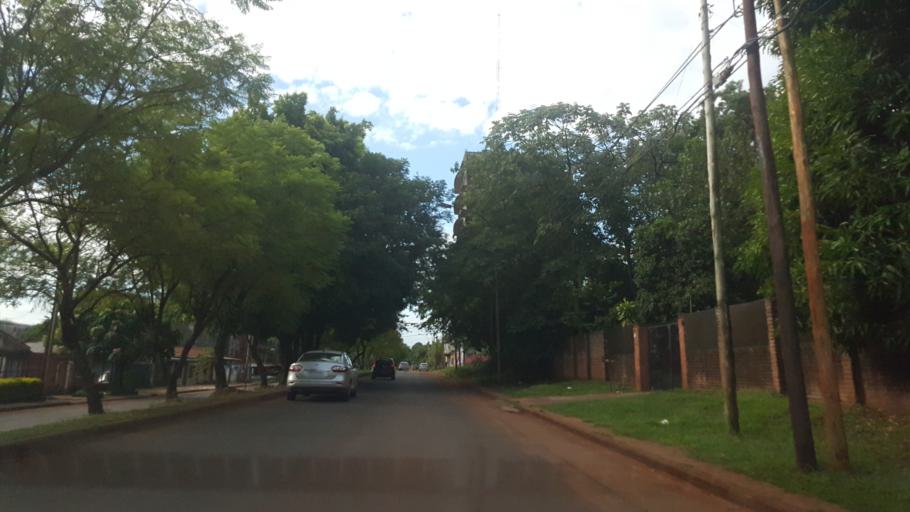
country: AR
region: Misiones
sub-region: Departamento de Capital
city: Posadas
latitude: -27.3731
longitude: -55.9325
